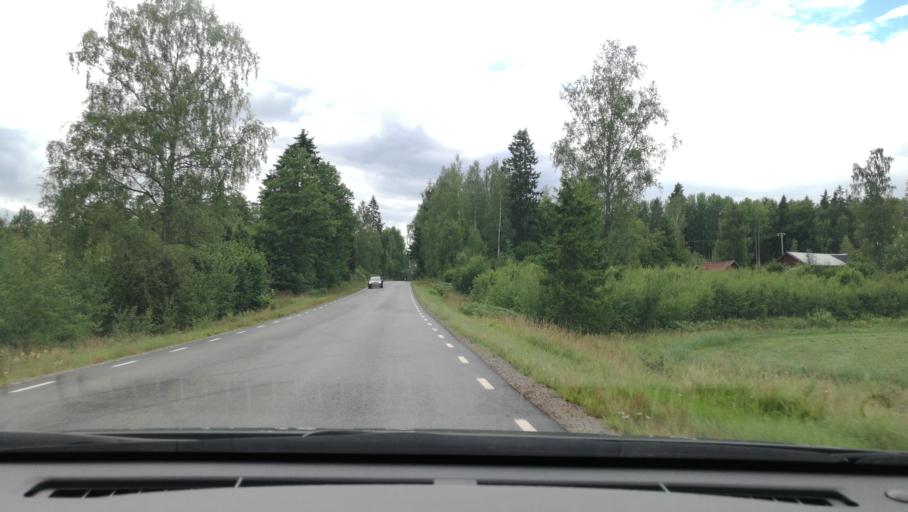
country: SE
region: OEstergoetland
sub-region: Norrkopings Kommun
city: Svartinge
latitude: 58.8229
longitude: 15.9920
